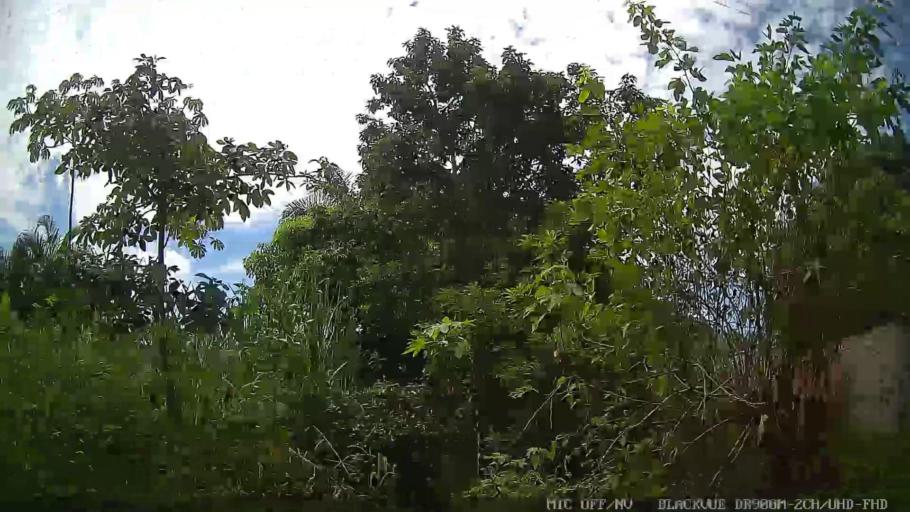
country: BR
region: Sao Paulo
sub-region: Iguape
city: Iguape
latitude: -24.7194
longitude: -47.5270
